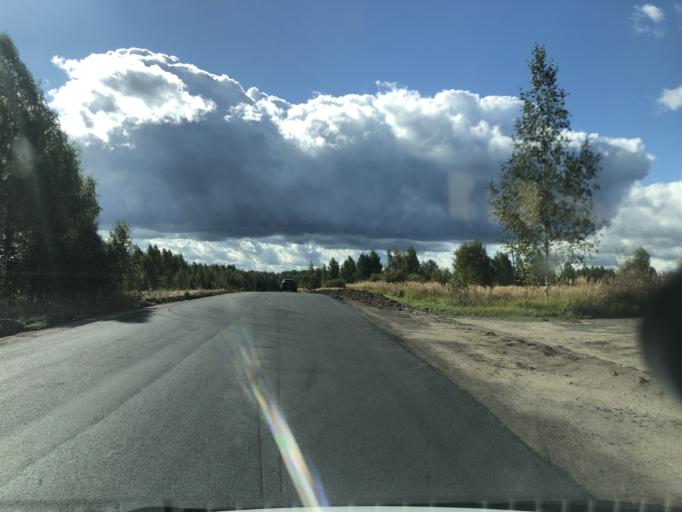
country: RU
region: Jaroslavl
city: Petrovsk
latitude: 56.9687
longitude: 39.3887
